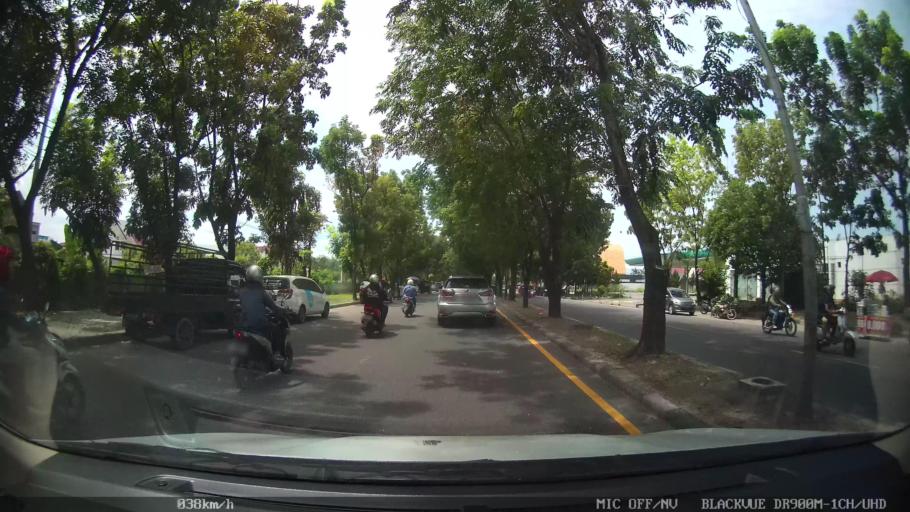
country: ID
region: North Sumatra
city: Sunggal
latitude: 3.5694
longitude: 98.6261
